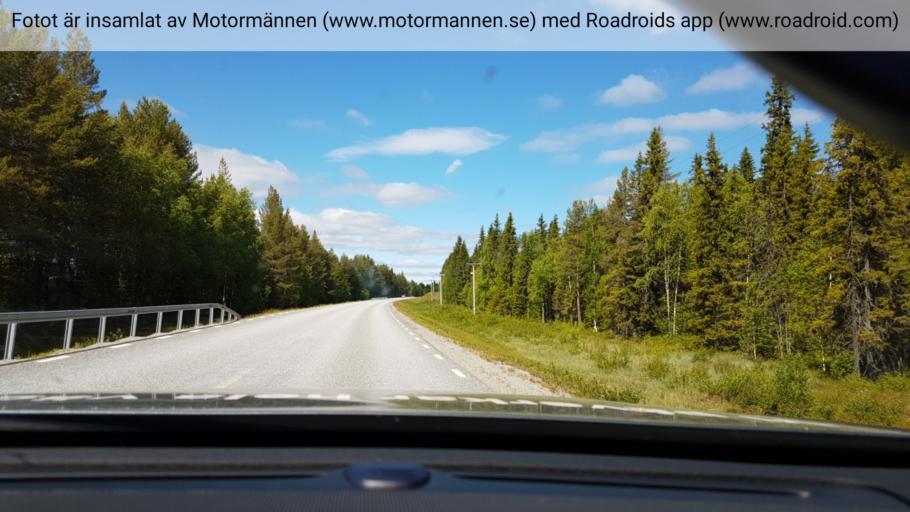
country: SE
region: Vaesterbotten
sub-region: Asele Kommun
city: Asele
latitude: 64.3404
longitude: 17.0290
